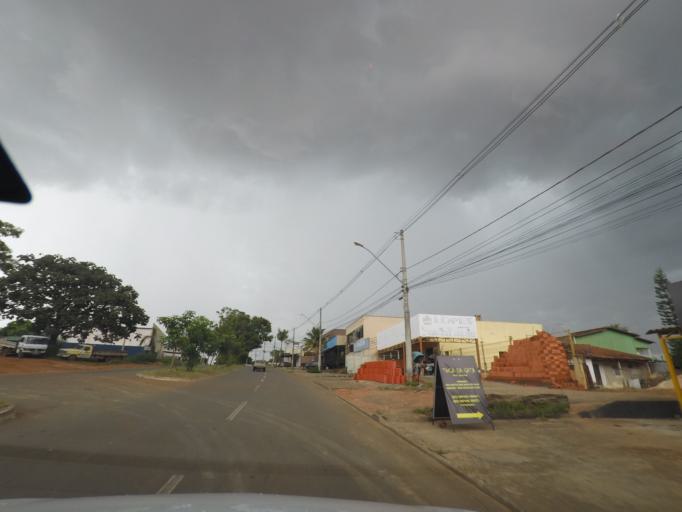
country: BR
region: Goias
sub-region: Goiania
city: Goiania
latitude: -16.7281
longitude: -49.3695
